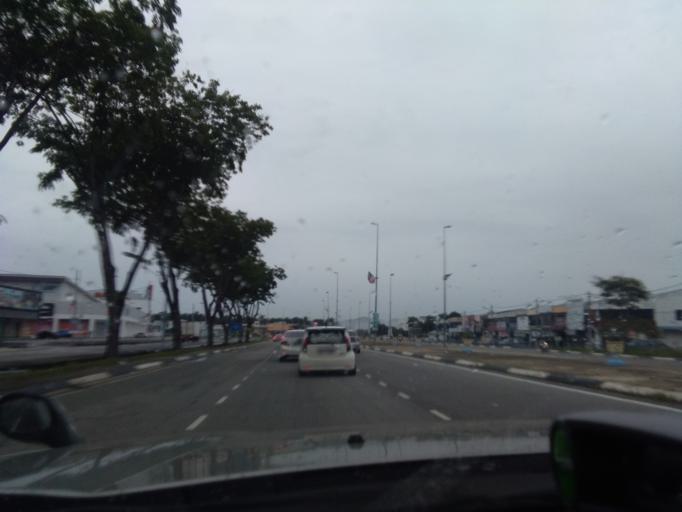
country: MY
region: Penang
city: Nibong Tebal
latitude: 5.1771
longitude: 100.4820
